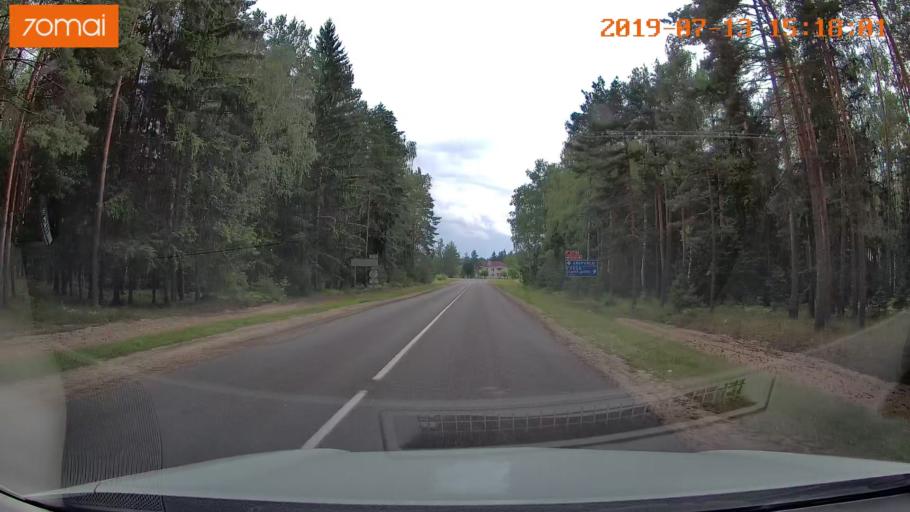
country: BY
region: Mogilev
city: Hlusha
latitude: 53.0886
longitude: 28.8461
